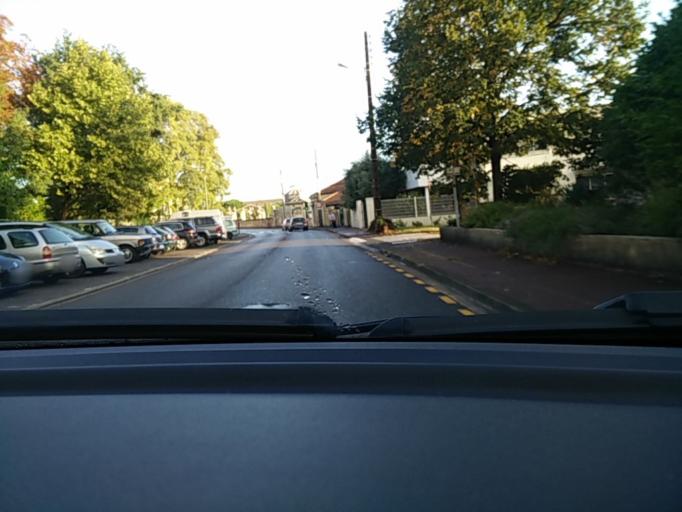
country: FR
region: Aquitaine
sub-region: Departement de la Gironde
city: Le Bouscat
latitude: 44.8653
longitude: -0.5949
